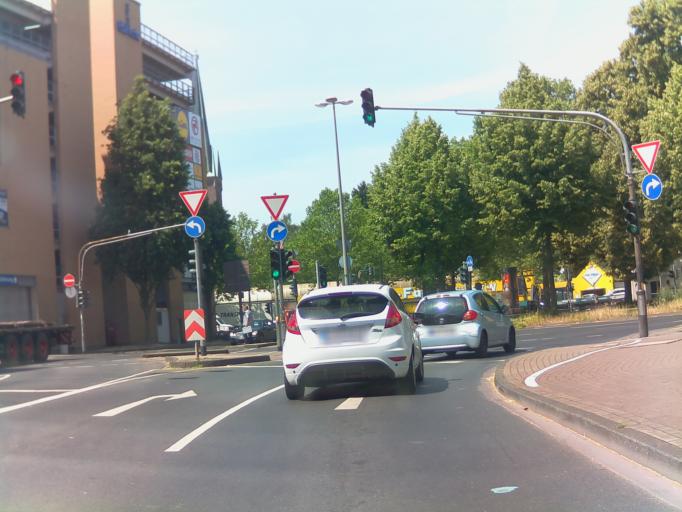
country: DE
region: North Rhine-Westphalia
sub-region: Regierungsbezirk Koln
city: Muelheim
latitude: 50.9635
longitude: 7.0071
